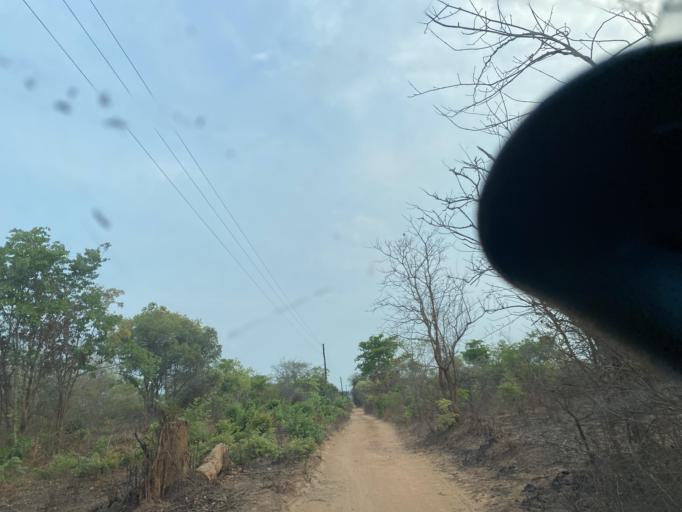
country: ZM
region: Lusaka
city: Chongwe
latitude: -15.2008
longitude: 28.4956
